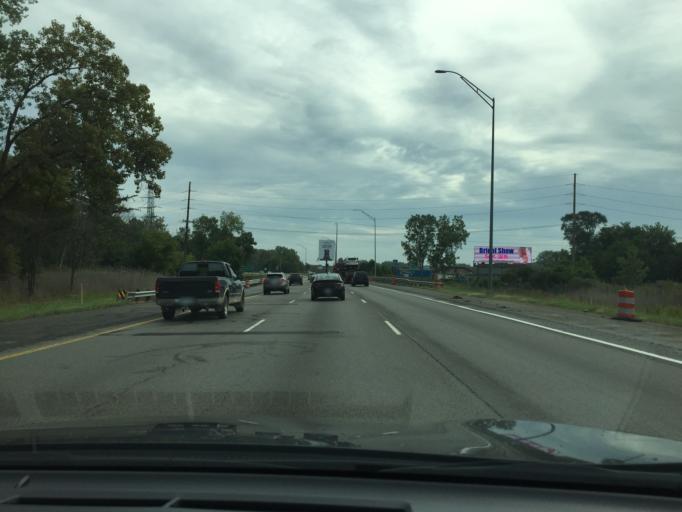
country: US
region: Michigan
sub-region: Wayne County
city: Taylor
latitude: 42.2467
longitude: -83.3100
